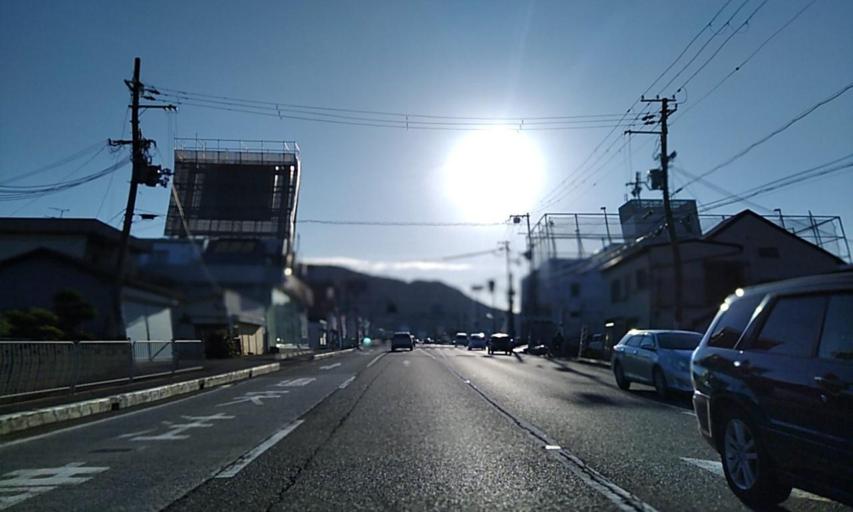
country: JP
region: Wakayama
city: Minato
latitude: 34.1884
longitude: 135.1767
